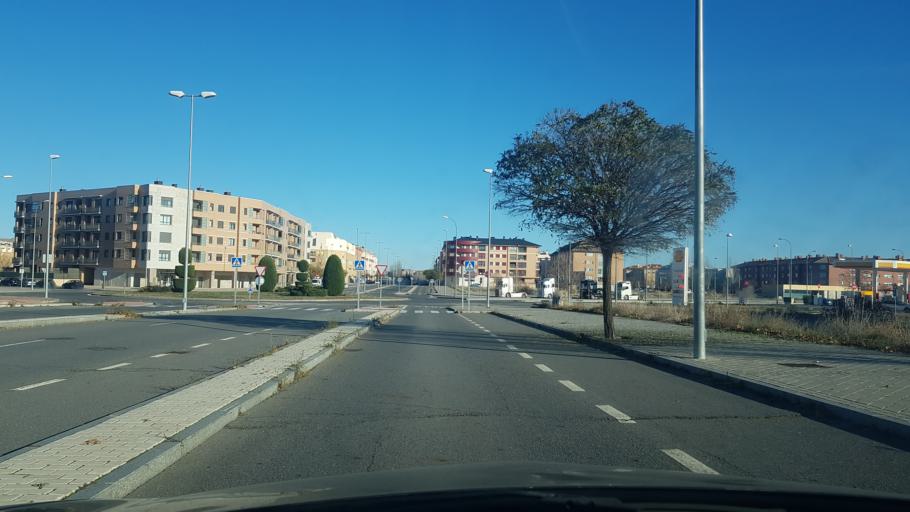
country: ES
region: Castille and Leon
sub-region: Provincia de Avila
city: Avila
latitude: 40.6415
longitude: -4.6973
